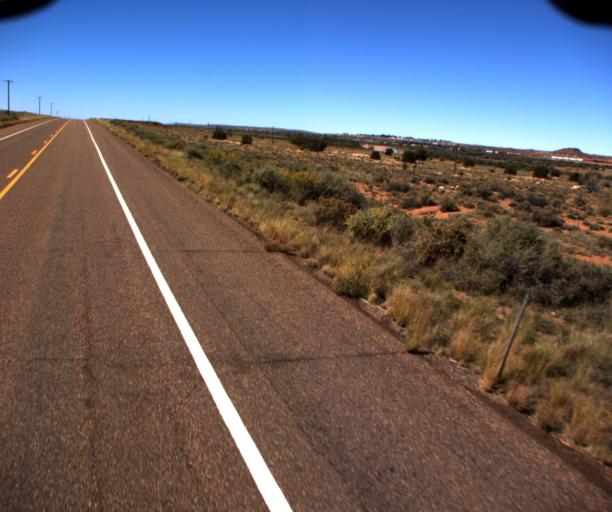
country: US
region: Arizona
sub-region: Navajo County
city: Holbrook
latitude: 34.8840
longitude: -110.1216
